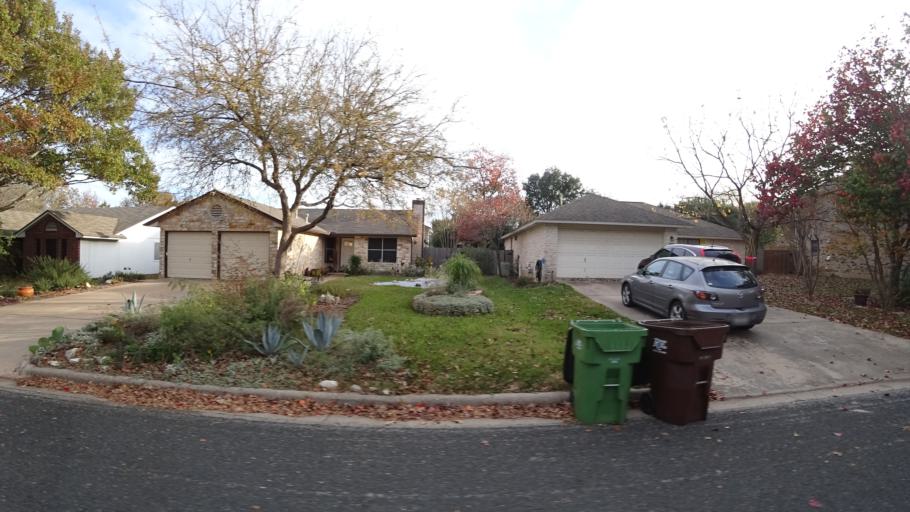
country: US
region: Texas
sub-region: Williamson County
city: Brushy Creek
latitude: 30.5144
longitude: -97.7256
